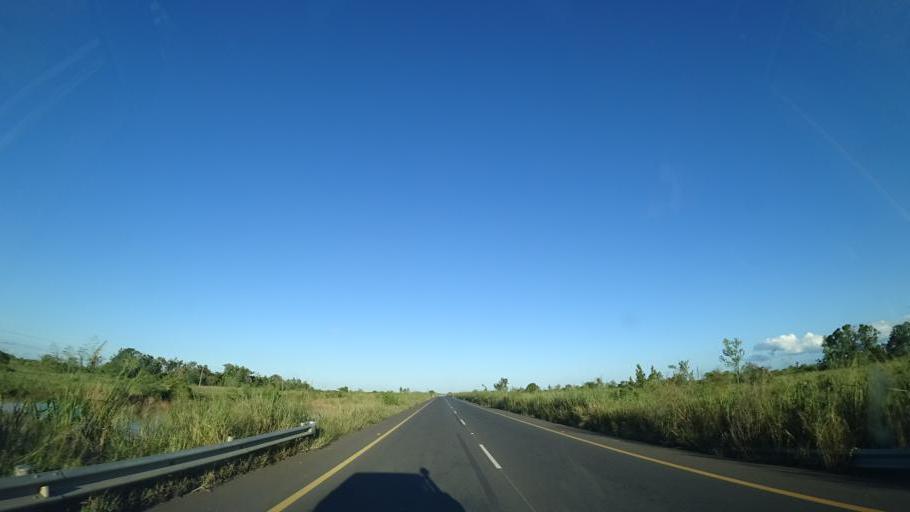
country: MZ
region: Sofala
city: Dondo
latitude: -19.3133
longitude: 34.2781
